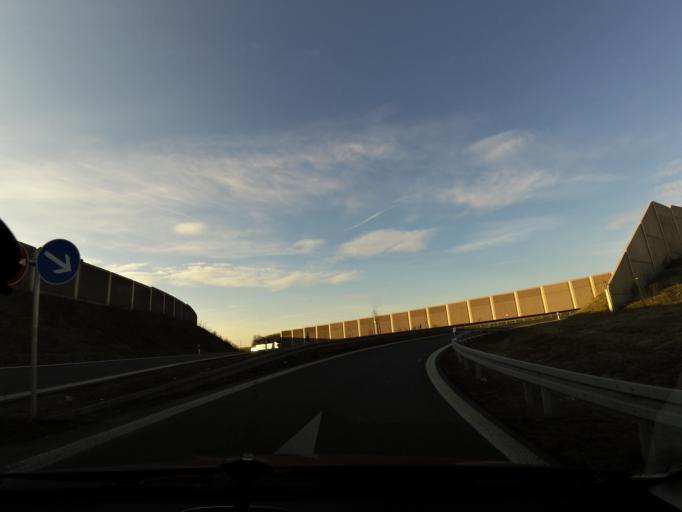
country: DE
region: Bavaria
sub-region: Regierungsbezirk Unterfranken
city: Kist
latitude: 49.7480
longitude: 9.8430
